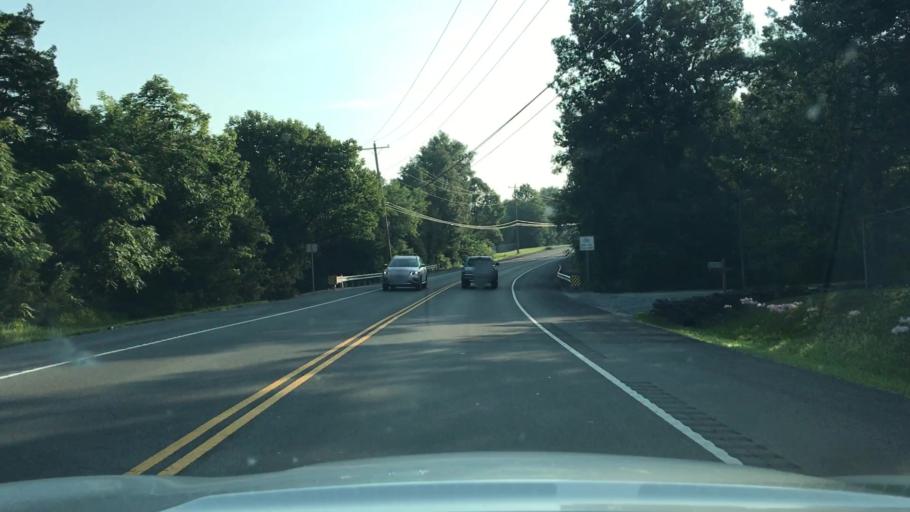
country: US
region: Tennessee
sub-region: Rutherford County
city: La Vergne
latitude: 36.0672
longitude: -86.5878
